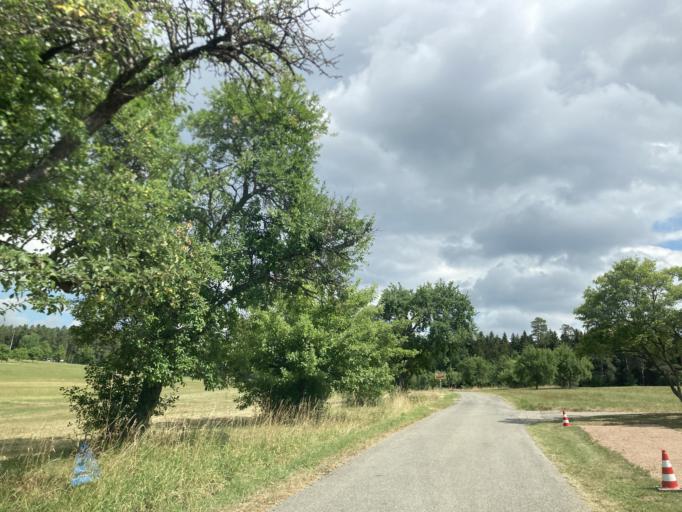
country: DE
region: Baden-Wuerttemberg
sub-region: Karlsruhe Region
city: Ebhausen
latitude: 48.6085
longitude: 8.6597
